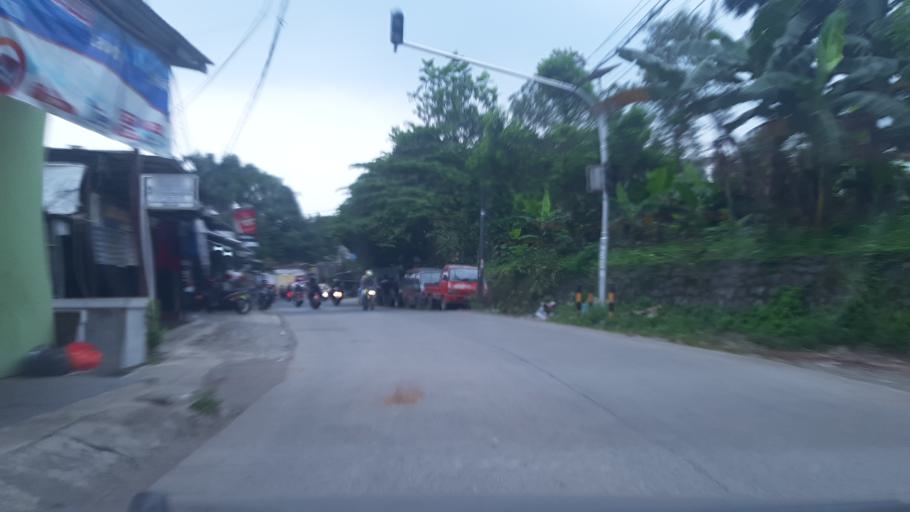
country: ID
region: West Java
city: Bogor
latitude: -6.5705
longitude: 106.8652
